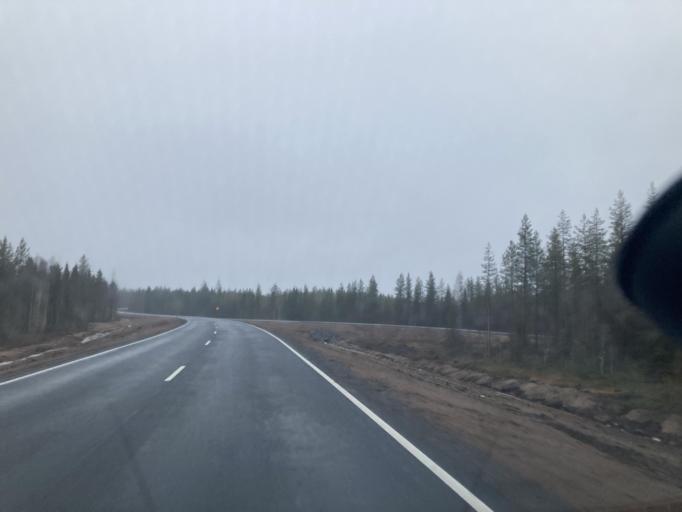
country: FI
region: Lapland
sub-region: Rovaniemi
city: Rovaniemi
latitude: 66.5895
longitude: 25.7993
